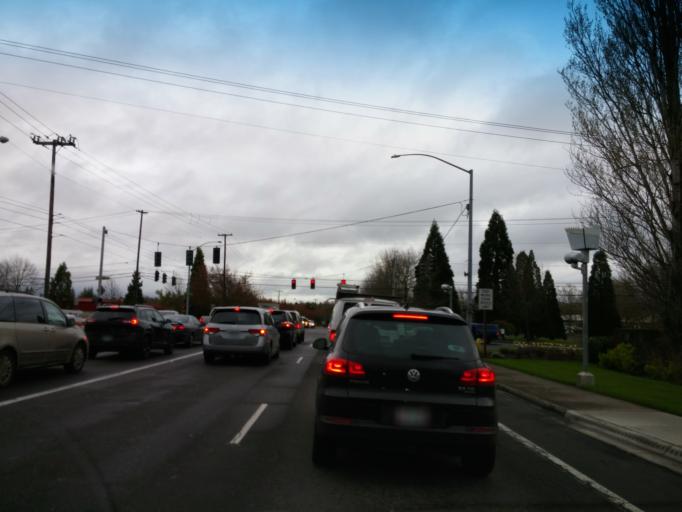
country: US
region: Oregon
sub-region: Washington County
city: Oak Hills
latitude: 45.5163
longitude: -122.8395
